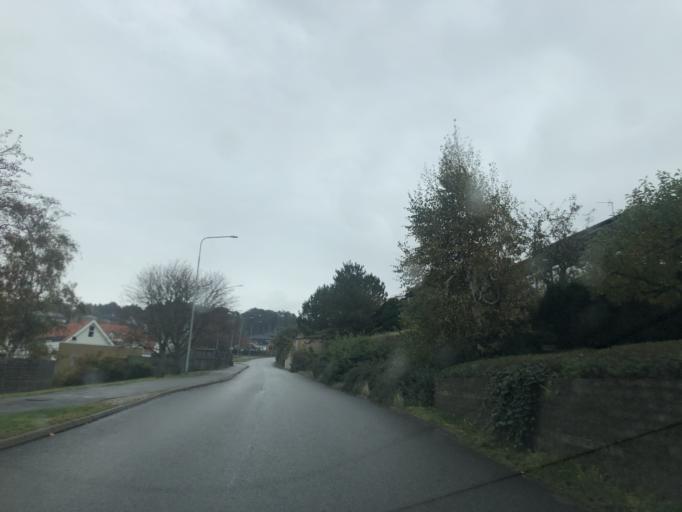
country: SE
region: Vaestra Goetaland
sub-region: Goteborg
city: Majorna
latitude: 57.6326
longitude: 11.9184
